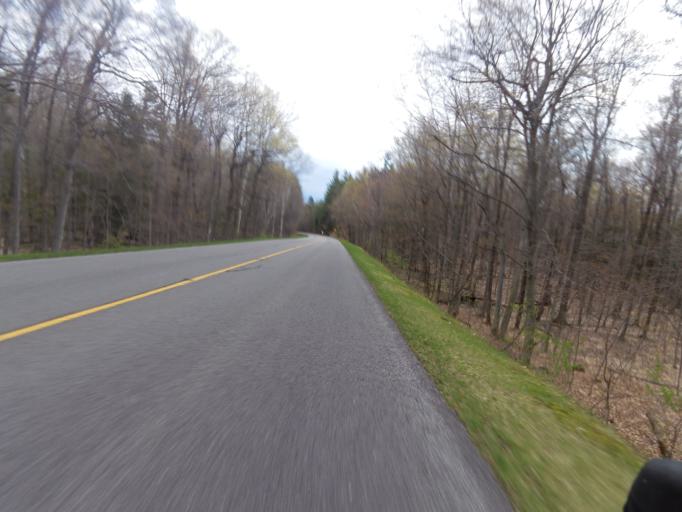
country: CA
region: Quebec
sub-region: Outaouais
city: Gatineau
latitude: 45.4707
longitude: -75.8366
